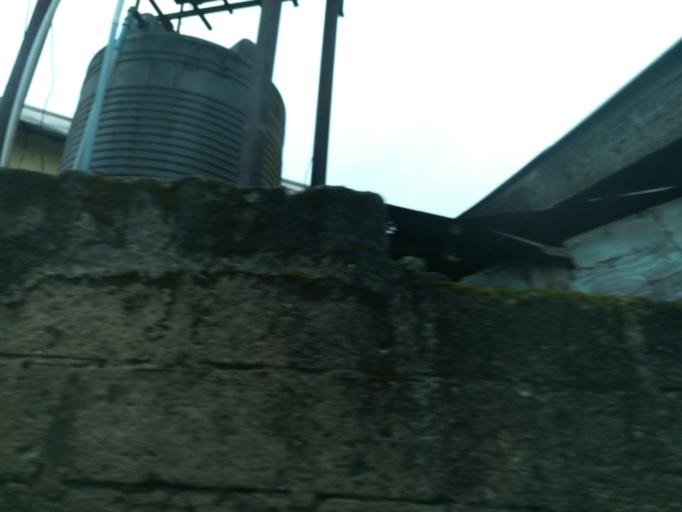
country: NG
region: Rivers
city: Port Harcourt
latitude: 4.8159
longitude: 7.0197
